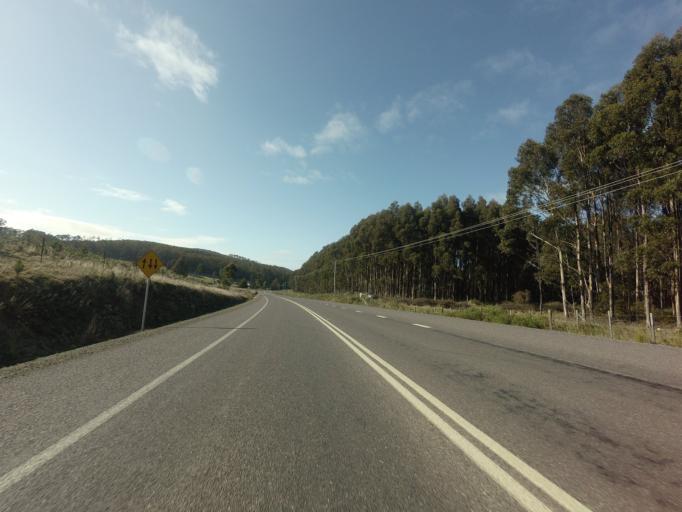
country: AU
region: Tasmania
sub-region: Huon Valley
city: Geeveston
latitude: -43.2548
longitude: 146.9990
